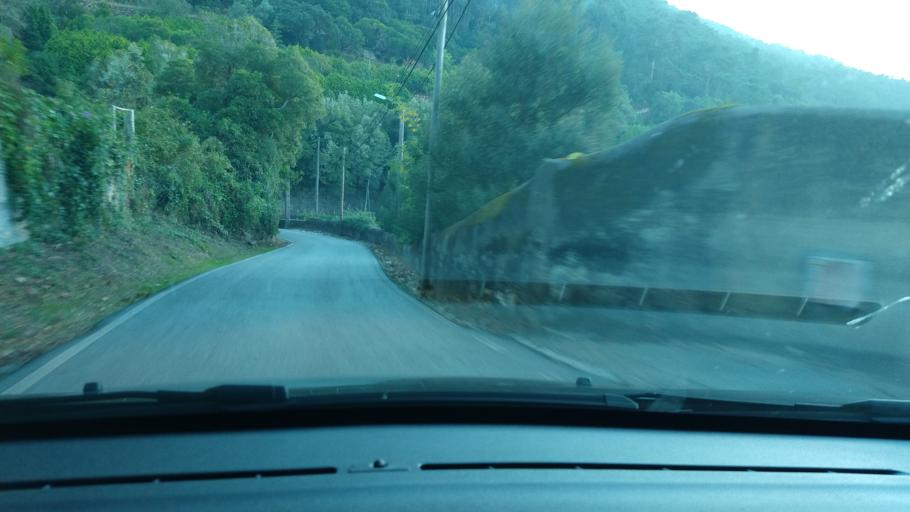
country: PT
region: Lisbon
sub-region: Sintra
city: Colares
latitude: 38.7960
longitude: -9.4312
